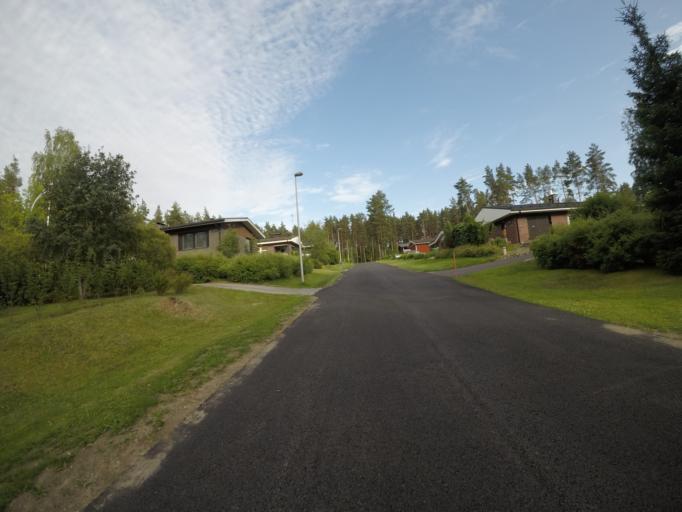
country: FI
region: Haeme
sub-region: Haemeenlinna
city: Haemeenlinna
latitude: 60.9724
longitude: 24.3957
